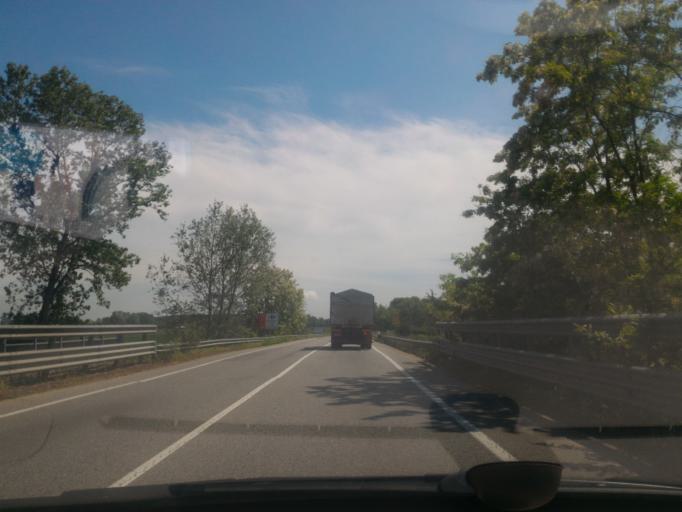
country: IT
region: Piedmont
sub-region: Provincia di Torino
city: Trofarello
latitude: 44.9564
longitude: 7.7133
